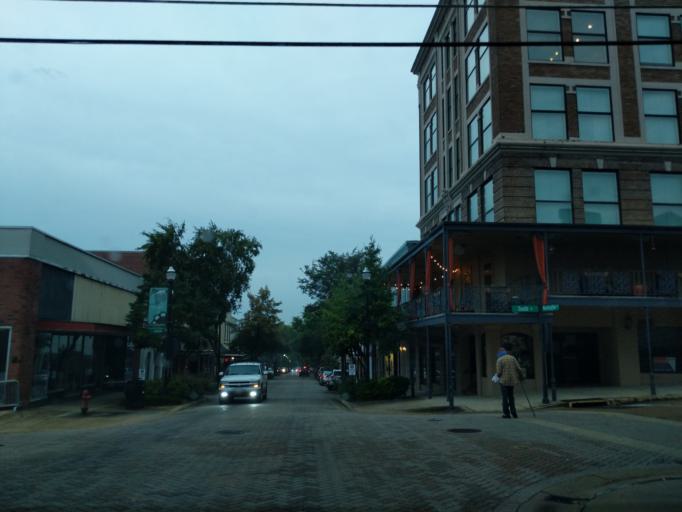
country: US
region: Mississippi
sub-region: Warren County
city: Vicksburg
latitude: 32.3480
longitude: -90.8825
